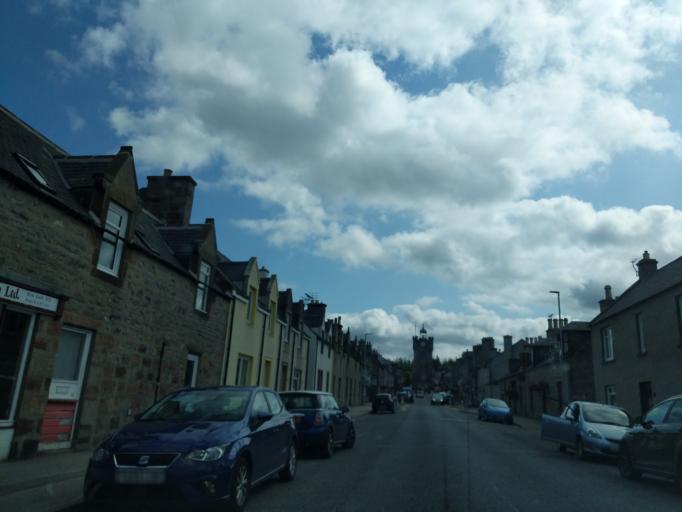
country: GB
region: Scotland
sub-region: Moray
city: Dufftown
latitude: 57.4466
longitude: -3.1289
